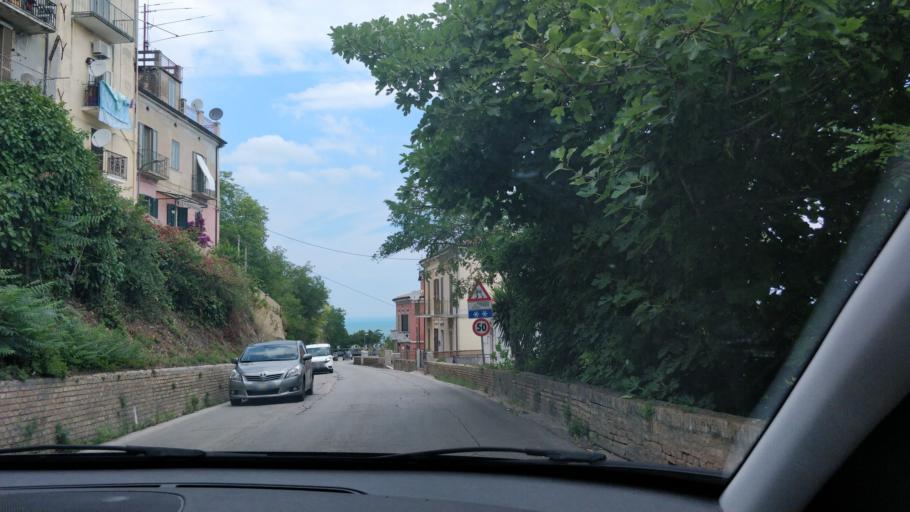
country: IT
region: Abruzzo
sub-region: Provincia di Chieti
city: Marina di San Vito
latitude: 42.3036
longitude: 14.4465
